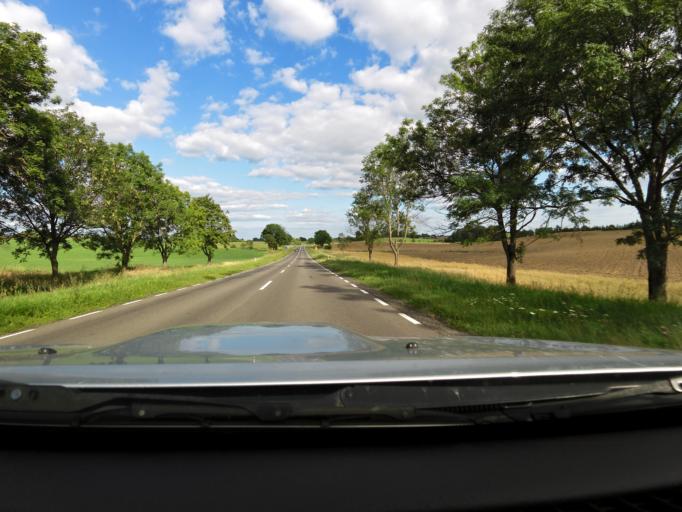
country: PL
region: Podlasie
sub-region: Powiat suwalski
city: Raczki
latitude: 53.8582
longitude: 22.7519
